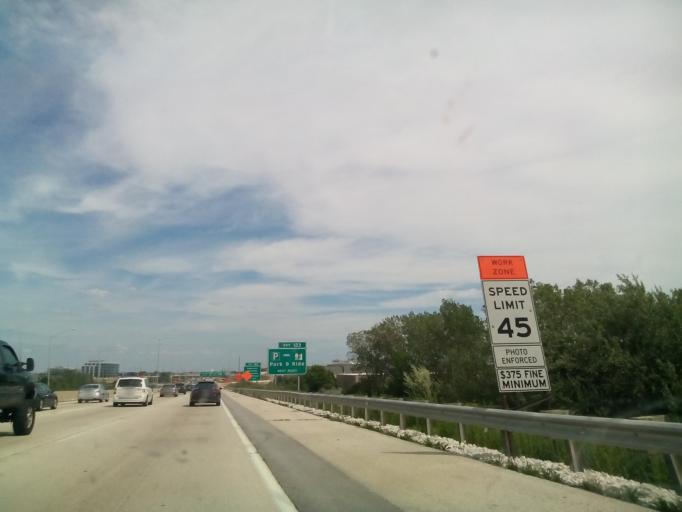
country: US
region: Illinois
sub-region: DuPage County
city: Warrenville
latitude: 41.8027
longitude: -88.2141
